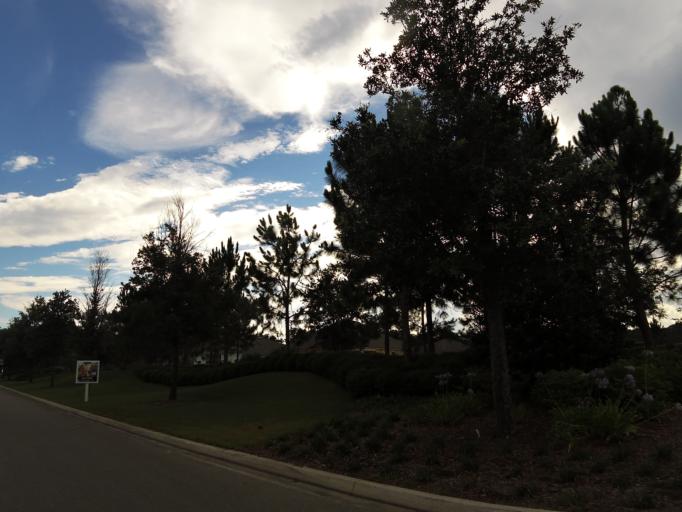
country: US
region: Florida
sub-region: Clay County
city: Green Cove Springs
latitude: 30.0223
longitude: -81.6383
